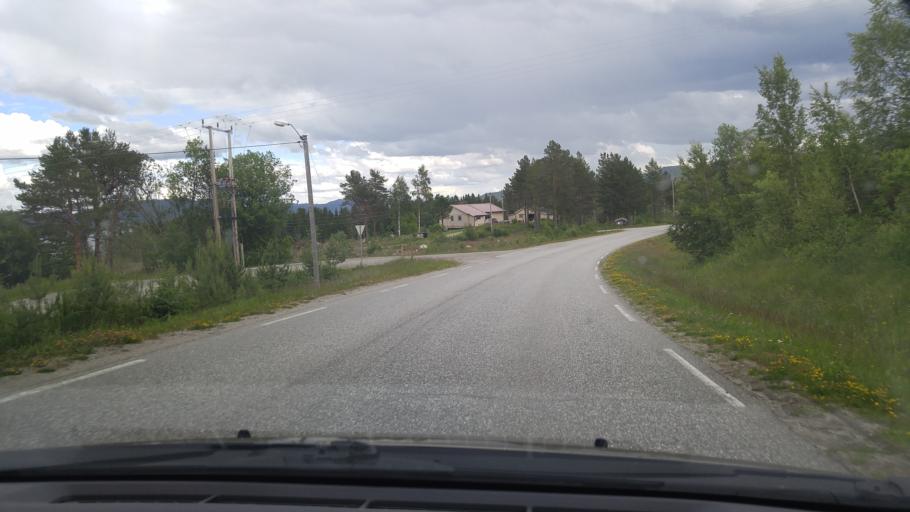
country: NO
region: Nord-Trondelag
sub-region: Naeroy
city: Kolvereid
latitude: 64.7676
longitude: 11.6144
